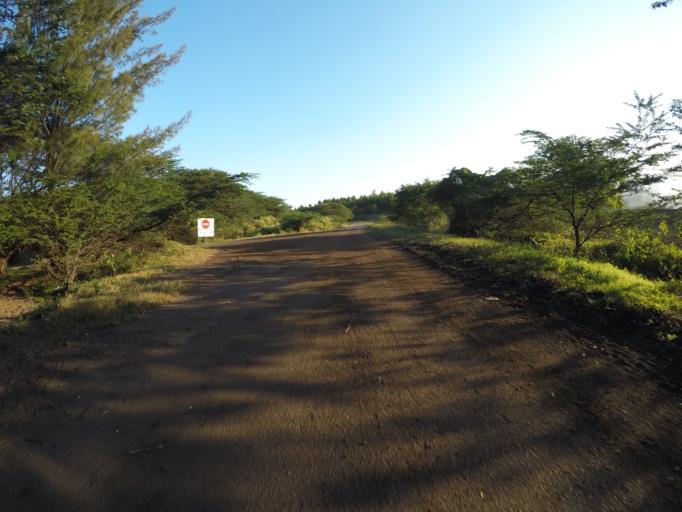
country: ZA
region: KwaZulu-Natal
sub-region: uThungulu District Municipality
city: KwaMbonambi
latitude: -28.6918
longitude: 32.2087
